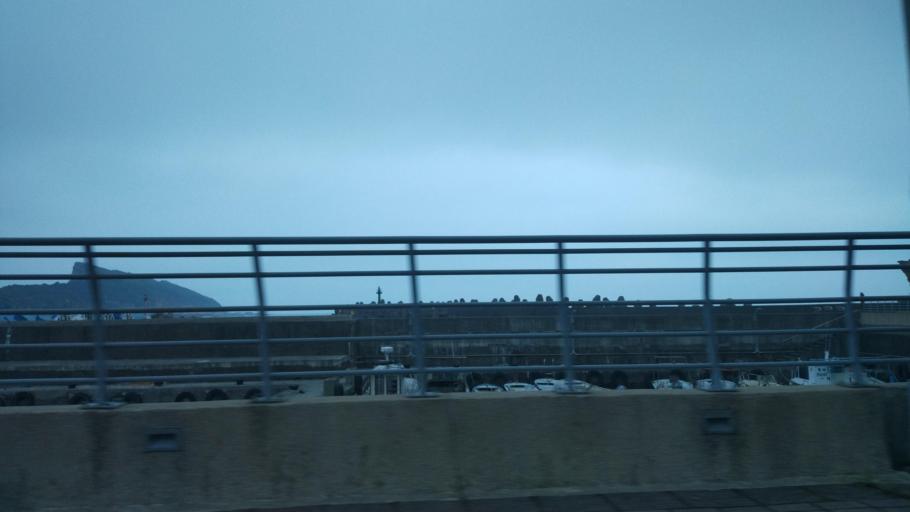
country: TW
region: Taiwan
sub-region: Keelung
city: Keelung
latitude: 25.2030
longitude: 121.6925
